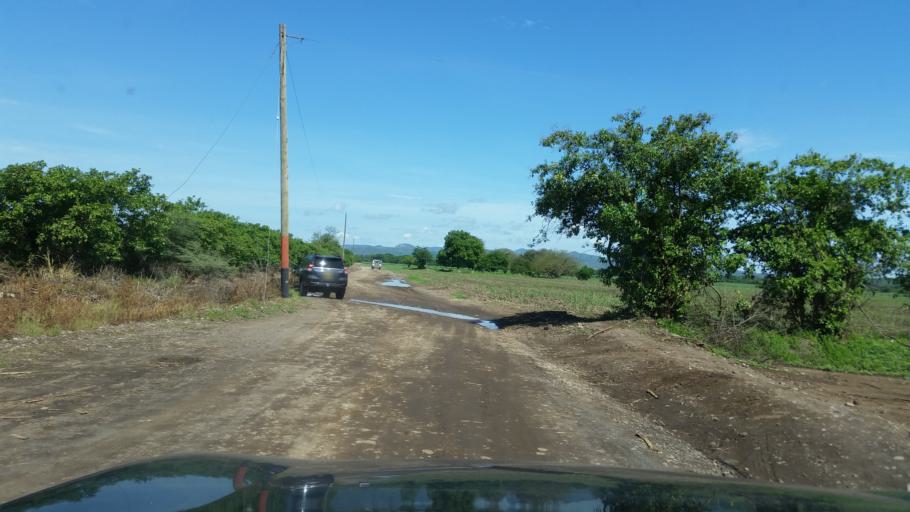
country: NI
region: Chinandega
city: Puerto Morazan
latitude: 12.7731
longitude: -87.1101
